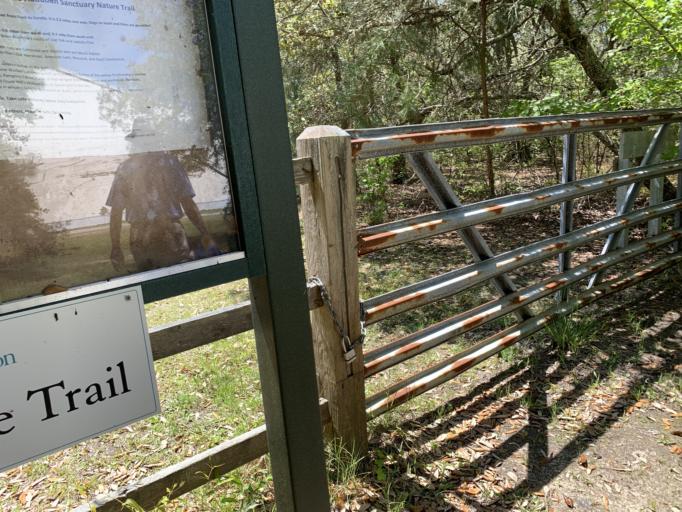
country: US
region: North Carolina
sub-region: Dare County
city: Southern Shores
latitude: 36.2564
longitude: -75.7892
